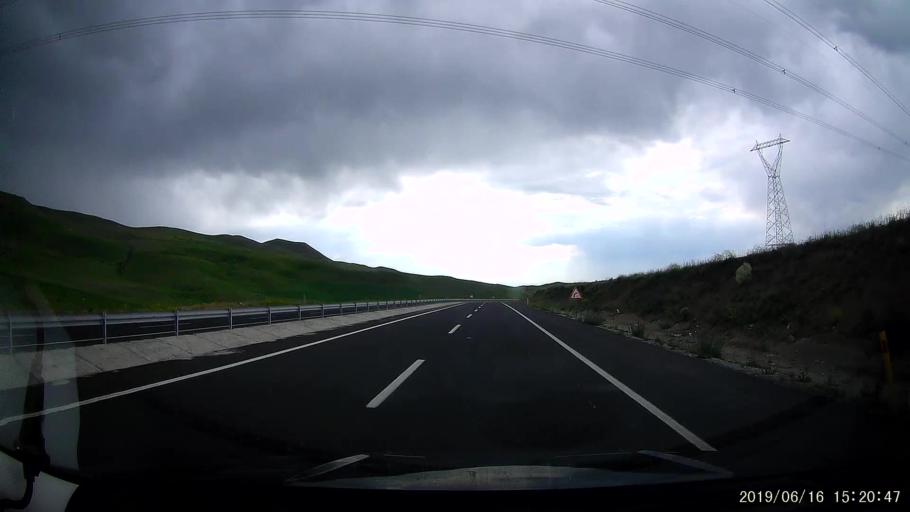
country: TR
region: Erzurum
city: Aras
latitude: 39.9730
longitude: 42.2573
